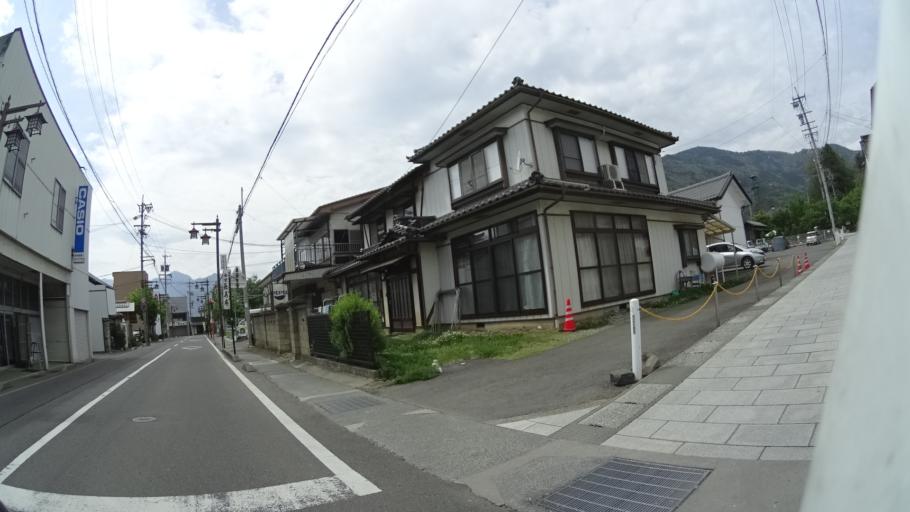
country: JP
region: Nagano
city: Ueda
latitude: 36.4628
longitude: 138.1826
